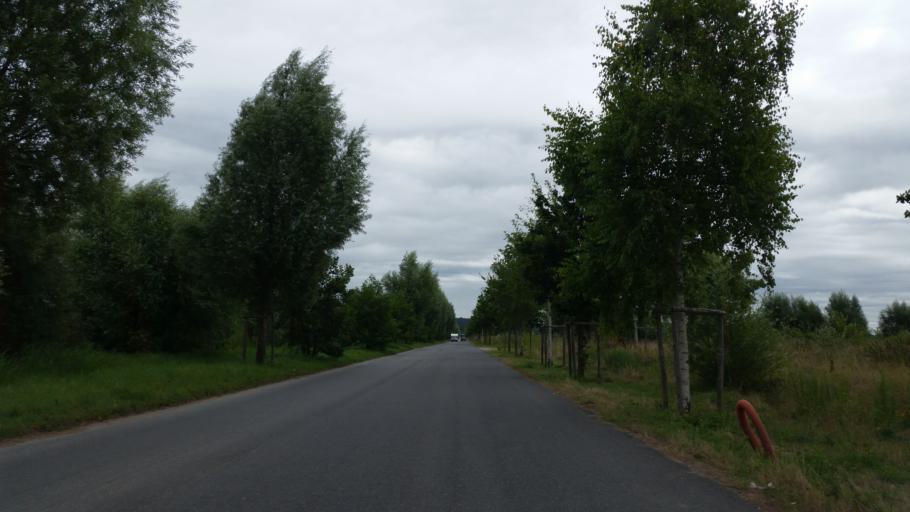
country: FR
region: Lower Normandy
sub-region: Departement du Calvados
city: La Riviere-Saint-Sauveur
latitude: 49.4199
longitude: 0.2623
